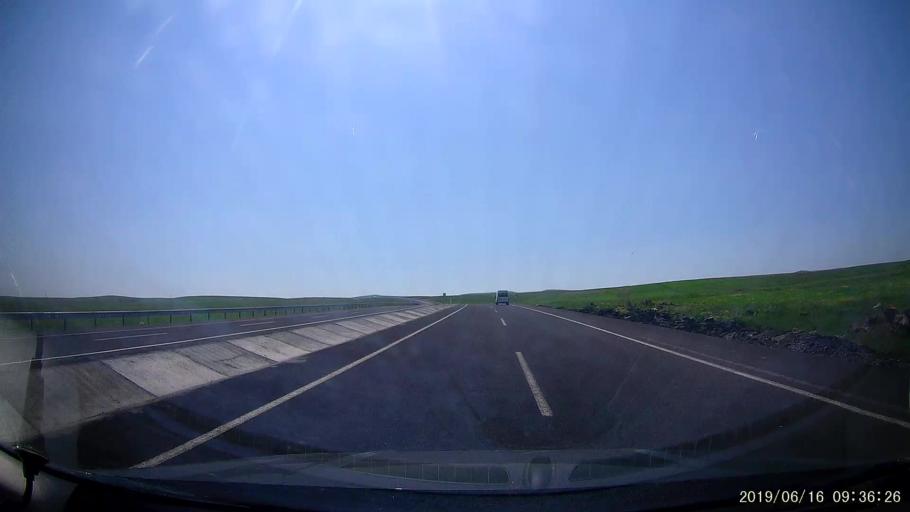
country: TR
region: Kars
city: Kars
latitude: 40.5579
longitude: 43.1726
